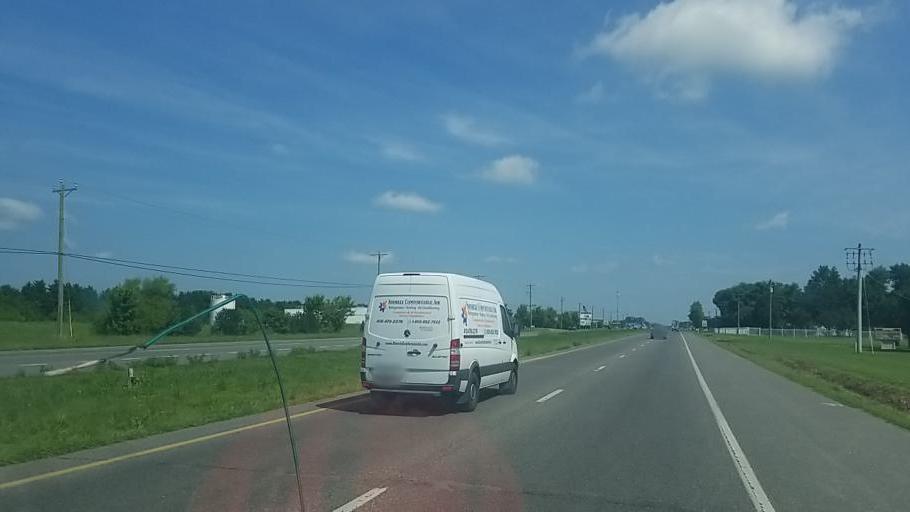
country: US
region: Delaware
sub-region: Sussex County
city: Seaford
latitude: 38.6865
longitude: -75.5906
